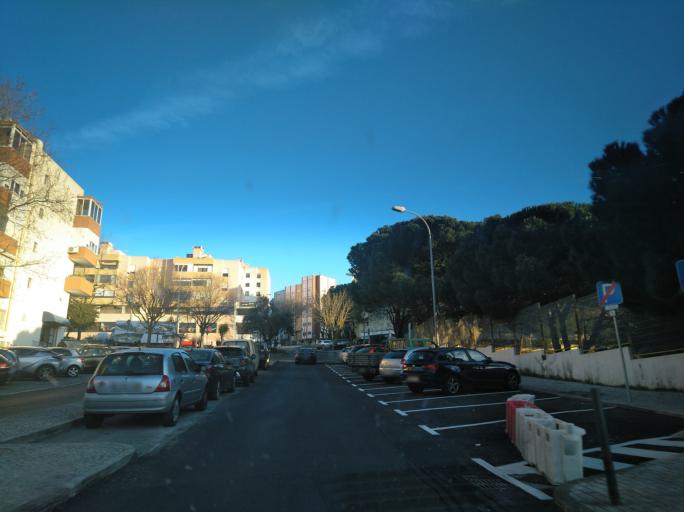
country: PT
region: Lisbon
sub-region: Amadora
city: Amadora
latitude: 38.7432
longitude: -9.2190
